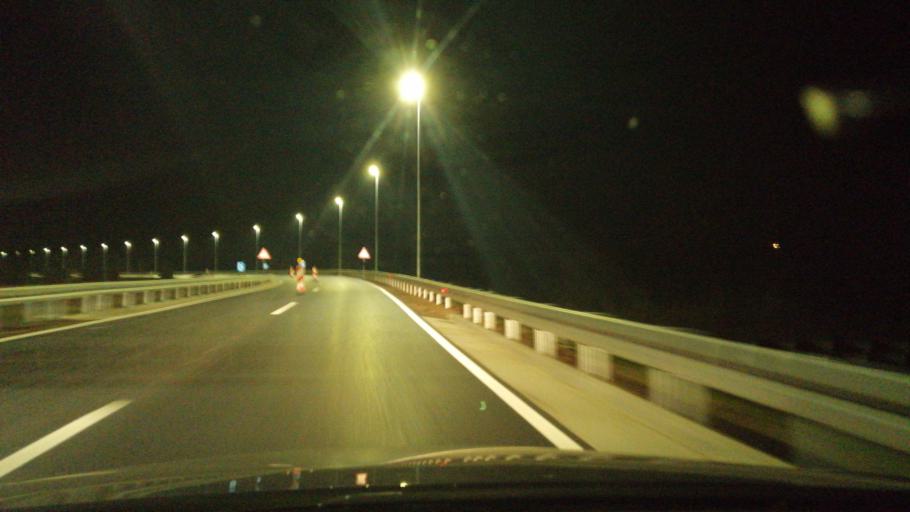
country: RS
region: Autonomna Pokrajina Vojvodina
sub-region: Juznobacki Okrug
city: Novi Sad
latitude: 45.3070
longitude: 19.8494
